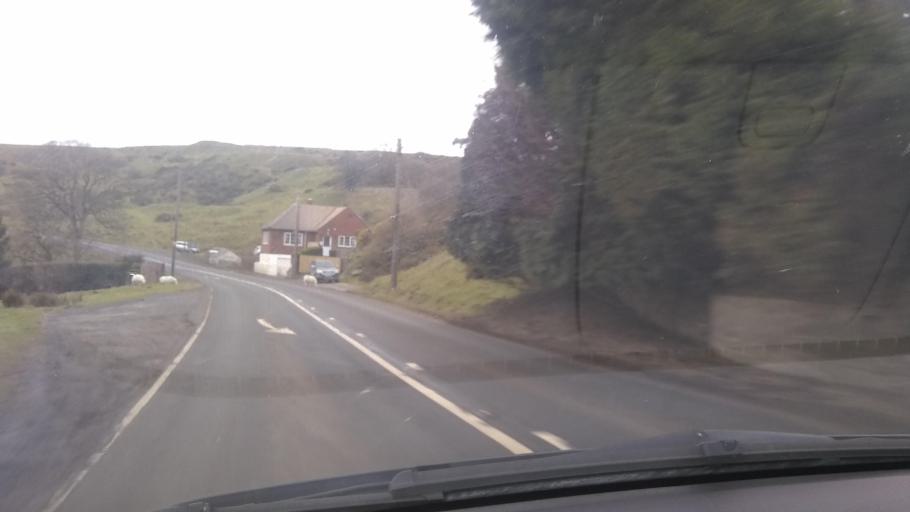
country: GB
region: England
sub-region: Worcestershire
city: Tenbury Wells
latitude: 52.3793
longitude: -2.5855
